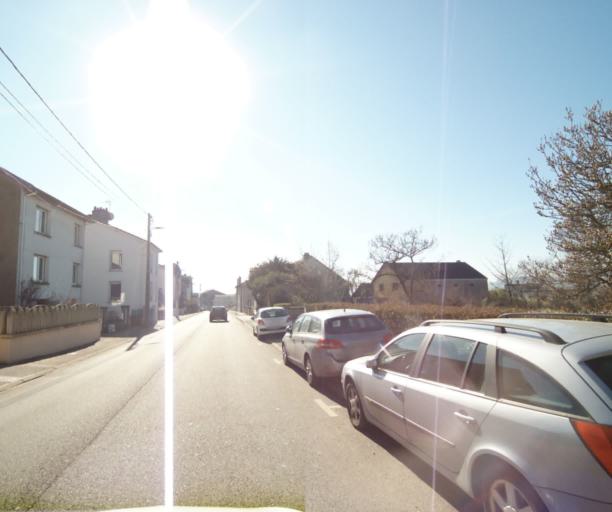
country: FR
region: Lorraine
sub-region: Departement de Meurthe-et-Moselle
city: Malzeville
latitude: 48.7216
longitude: 6.1813
